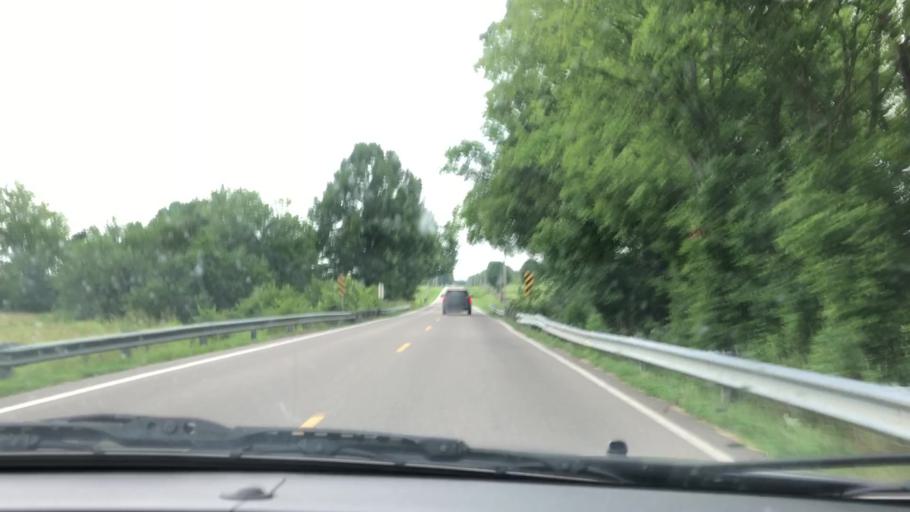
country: US
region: Tennessee
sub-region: Maury County
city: Spring Hill
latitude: 35.7308
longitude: -87.0111
